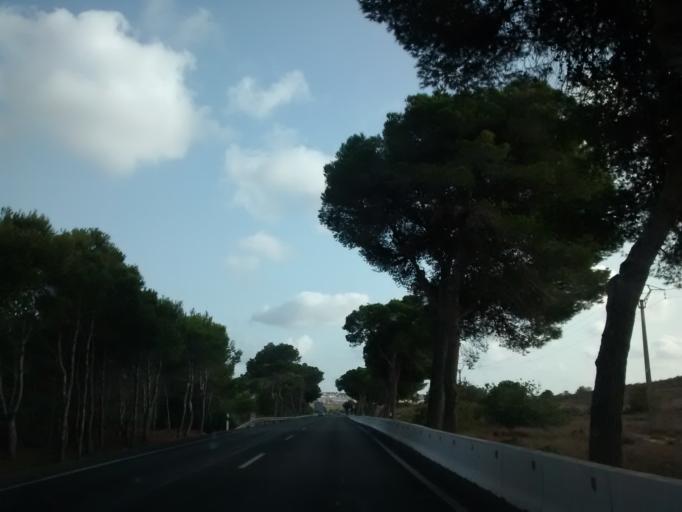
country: ES
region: Valencia
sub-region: Provincia de Alicante
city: Santa Pola
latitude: 38.2542
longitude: -0.5447
